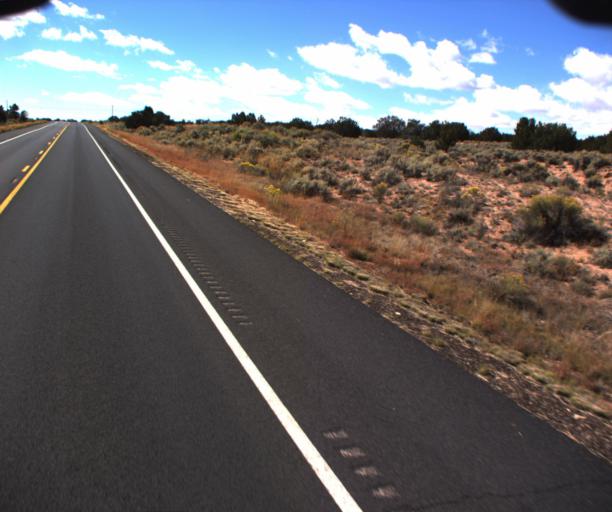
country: US
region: Arizona
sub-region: Apache County
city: Houck
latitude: 35.1848
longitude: -109.3365
